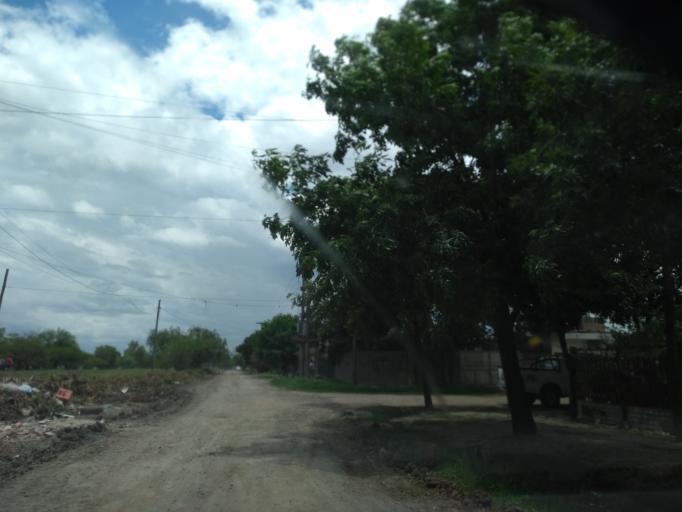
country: AR
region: Chaco
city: Resistencia
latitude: -27.4726
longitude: -58.9708
